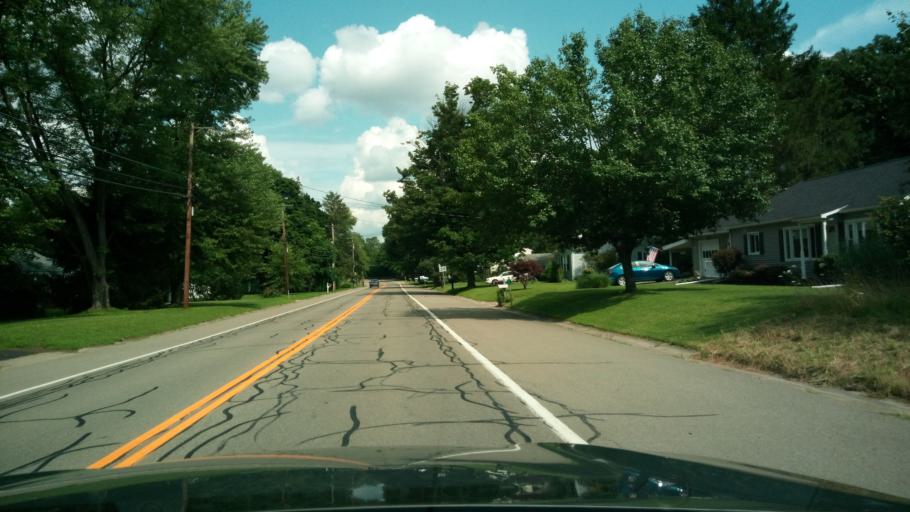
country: US
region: New York
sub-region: Chemung County
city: West Elmira
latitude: 42.0814
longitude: -76.8720
